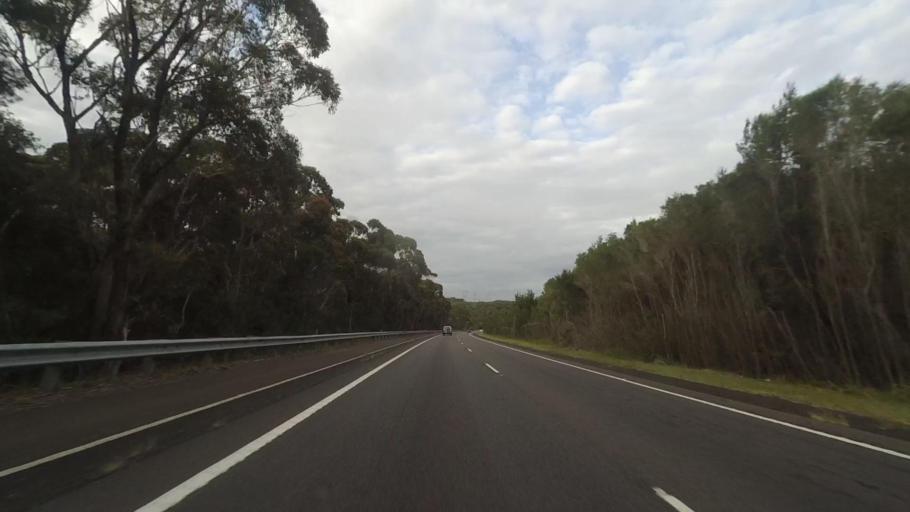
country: AU
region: New South Wales
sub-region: Wollongong
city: Helensburgh
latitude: -34.1676
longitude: 150.9784
